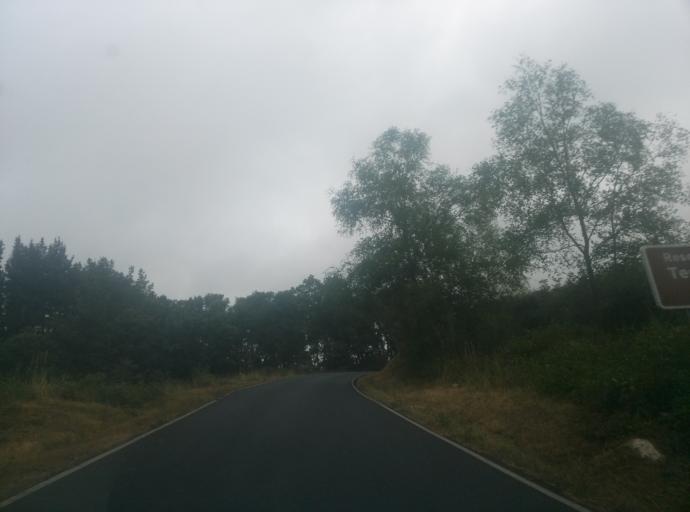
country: ES
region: Galicia
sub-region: Provincia de Lugo
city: Lugo
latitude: 43.0761
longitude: -7.5497
